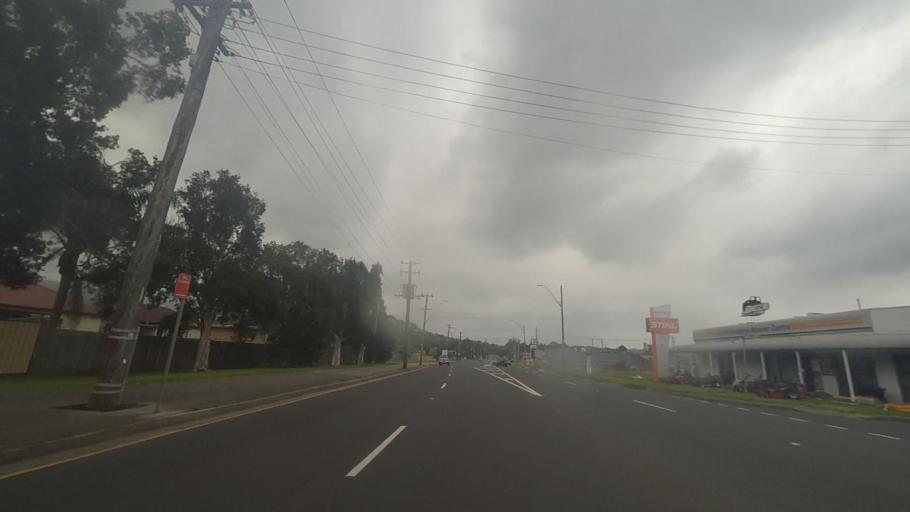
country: AU
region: New South Wales
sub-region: Wollongong
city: Cordeaux Heights
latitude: -34.4511
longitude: 150.8481
